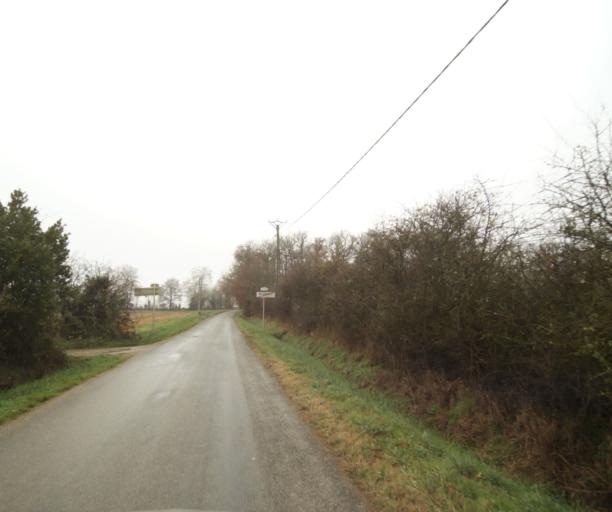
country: FR
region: Midi-Pyrenees
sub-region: Departement de la Haute-Garonne
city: Villaudric
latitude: 43.8538
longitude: 1.4605
